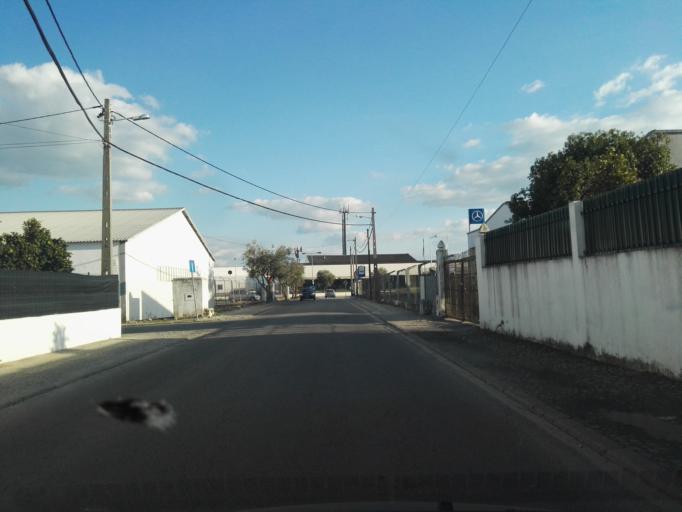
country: PT
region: Evora
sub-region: Evora
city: Evora
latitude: 38.5608
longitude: -7.9235
